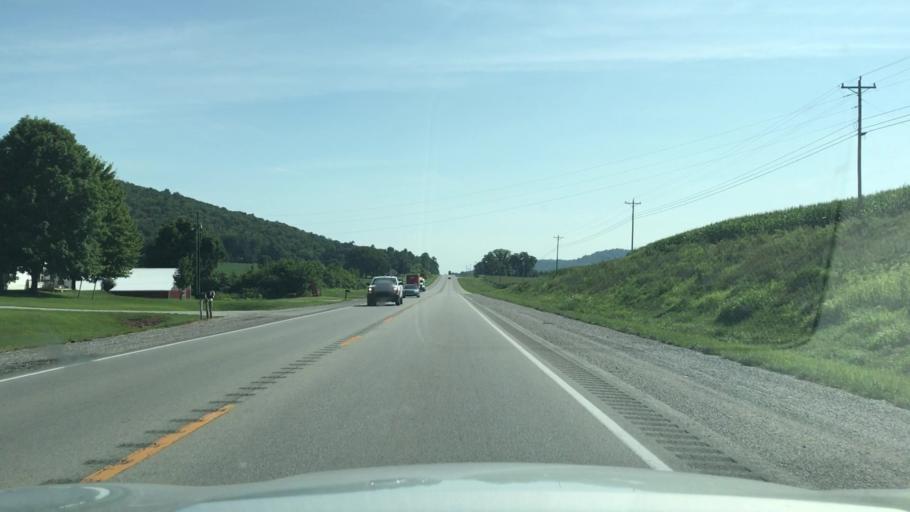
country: US
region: Kentucky
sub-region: Wayne County
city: Monticello
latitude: 36.7903
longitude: -84.9402
